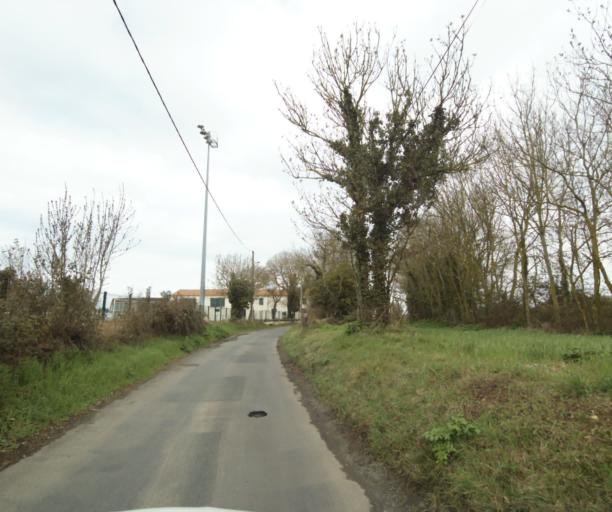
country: FR
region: Poitou-Charentes
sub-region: Departement de la Charente-Maritime
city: Lagord
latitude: 46.1900
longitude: -1.1673
